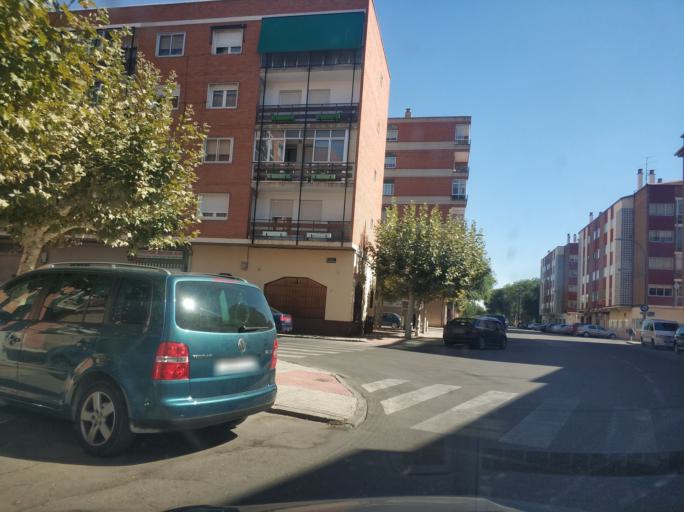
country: ES
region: Castille and Leon
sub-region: Provincia de Burgos
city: Aranda de Duero
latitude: 41.6702
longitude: -3.6771
